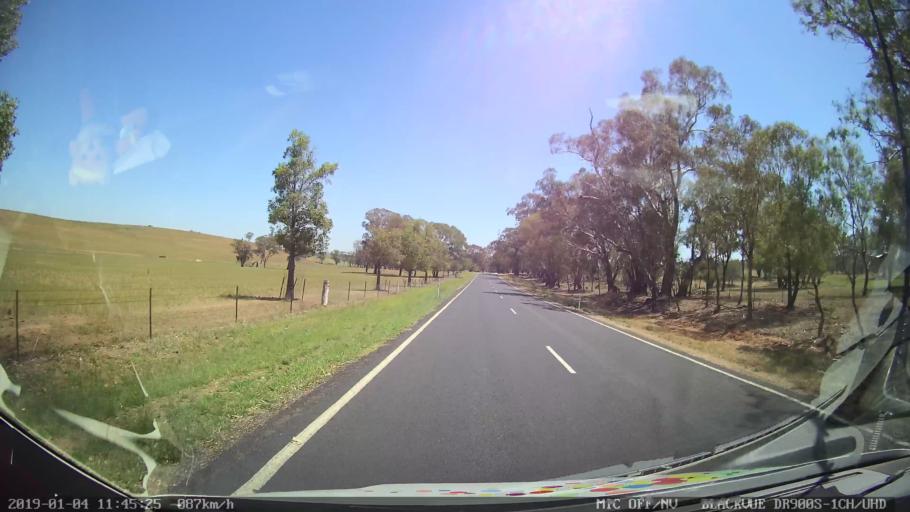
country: AU
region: New South Wales
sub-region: Cabonne
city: Molong
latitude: -32.9539
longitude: 148.7635
